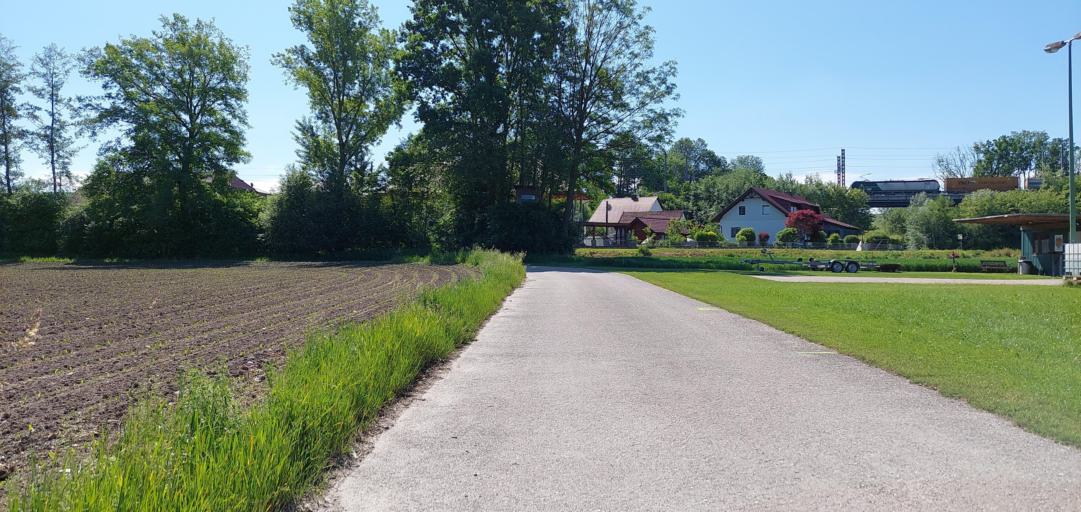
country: AT
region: Upper Austria
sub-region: Politischer Bezirk Grieskirchen
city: Bad Schallerbach
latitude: 48.2167
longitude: 13.9561
